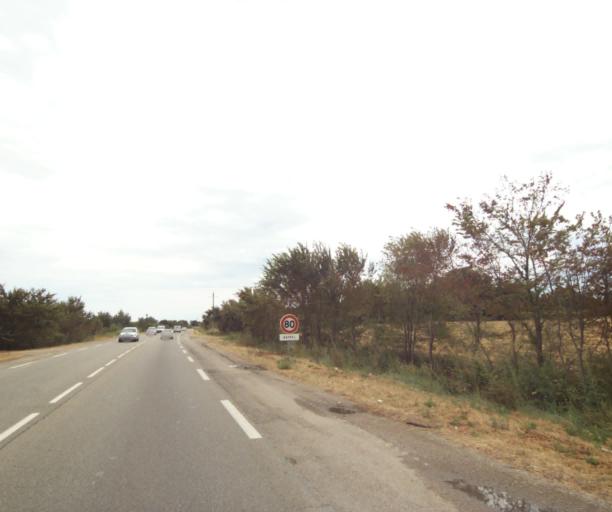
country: FR
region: Languedoc-Roussillon
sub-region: Departement de l'Herault
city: Saint-Just
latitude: 43.6428
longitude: 4.1387
